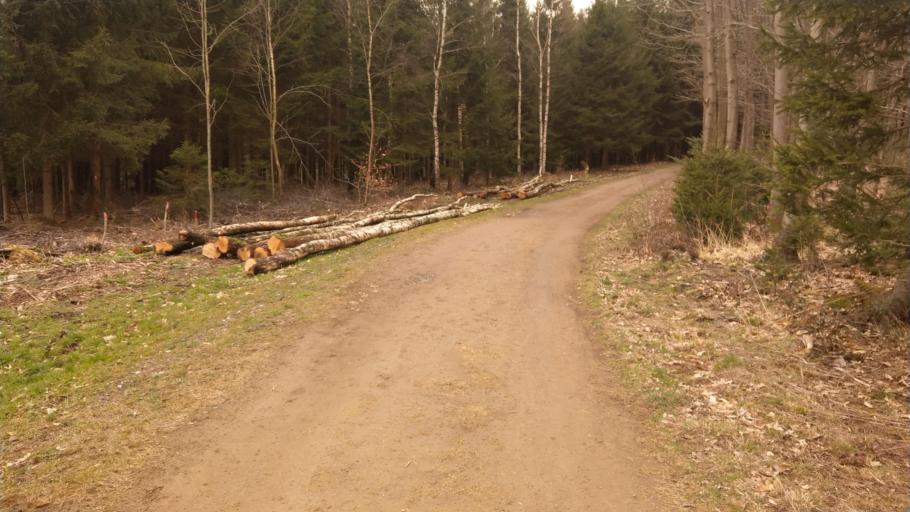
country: BE
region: Wallonia
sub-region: Province de Liege
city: La Calamine
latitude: 50.7190
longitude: 6.0581
